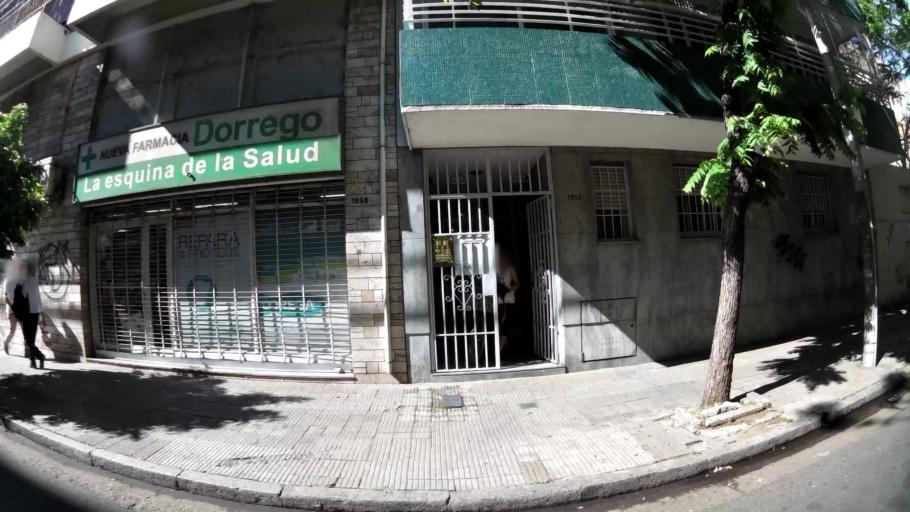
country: AR
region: Santa Fe
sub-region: Departamento de Rosario
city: Rosario
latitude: -32.9497
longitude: -60.6508
